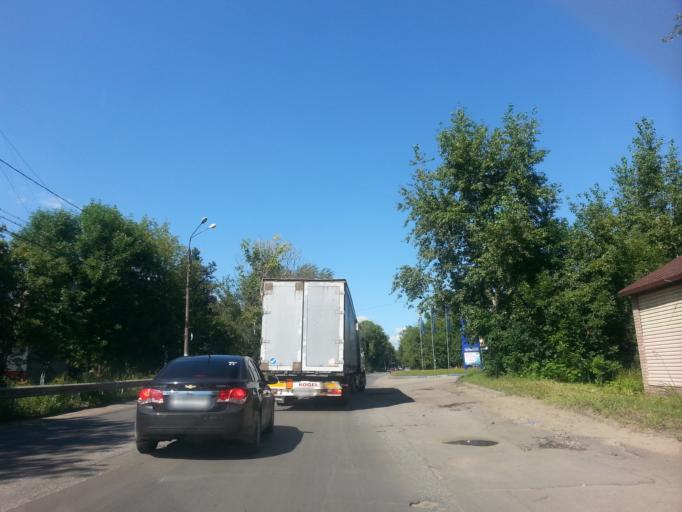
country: RU
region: Nizjnij Novgorod
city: Gorbatovka
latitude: 56.3357
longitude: 43.8482
